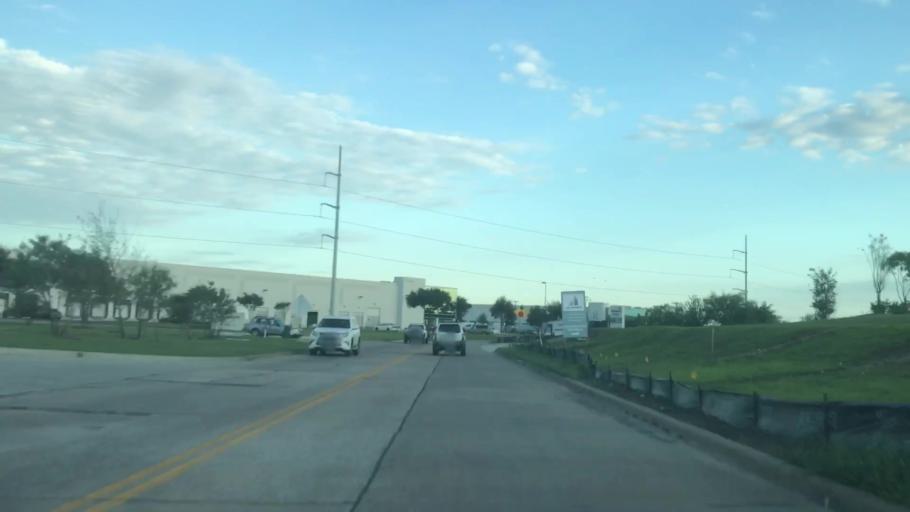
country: US
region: Texas
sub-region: Dallas County
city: Coppell
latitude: 32.9418
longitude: -97.0209
